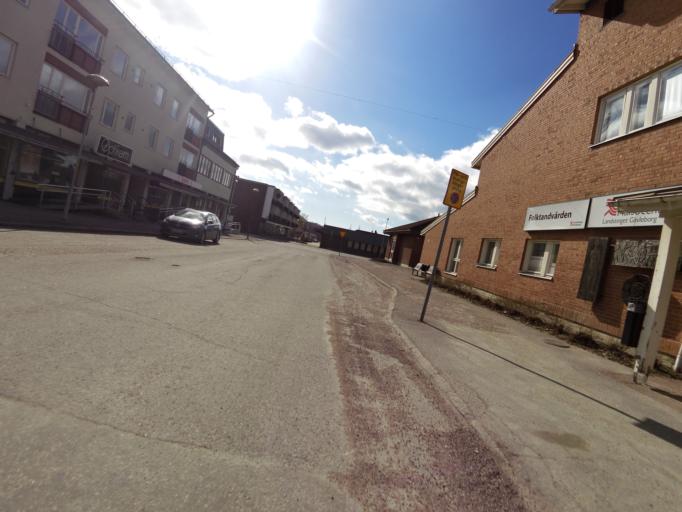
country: SE
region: Gaevleborg
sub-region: Hofors Kommun
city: Hofors
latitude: 60.5476
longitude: 16.2869
